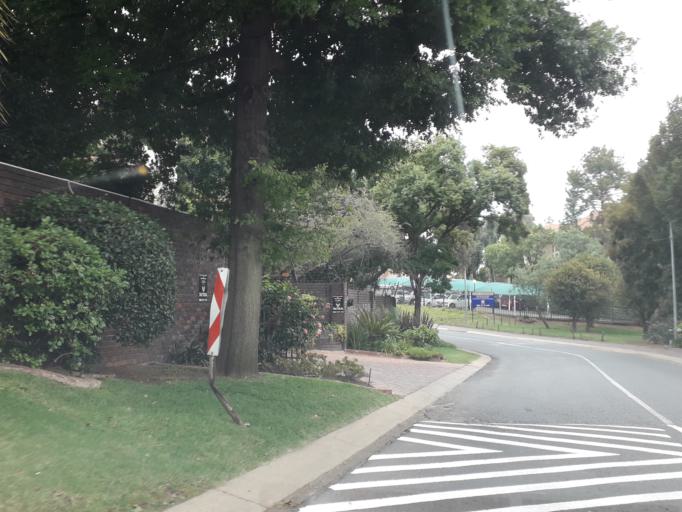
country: ZA
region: Gauteng
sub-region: City of Johannesburg Metropolitan Municipality
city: Modderfontein
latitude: -26.1069
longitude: 28.0712
